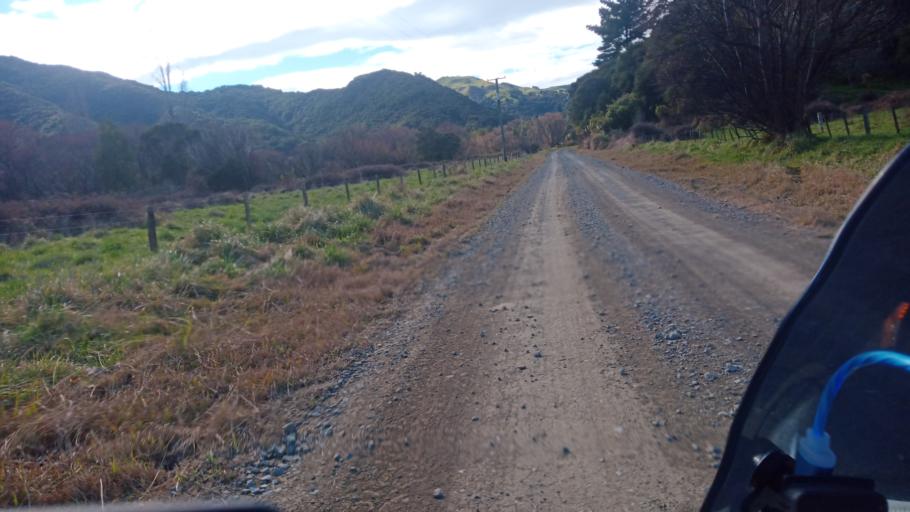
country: NZ
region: Gisborne
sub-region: Gisborne District
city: Gisborne
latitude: -38.2940
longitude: 178.2772
